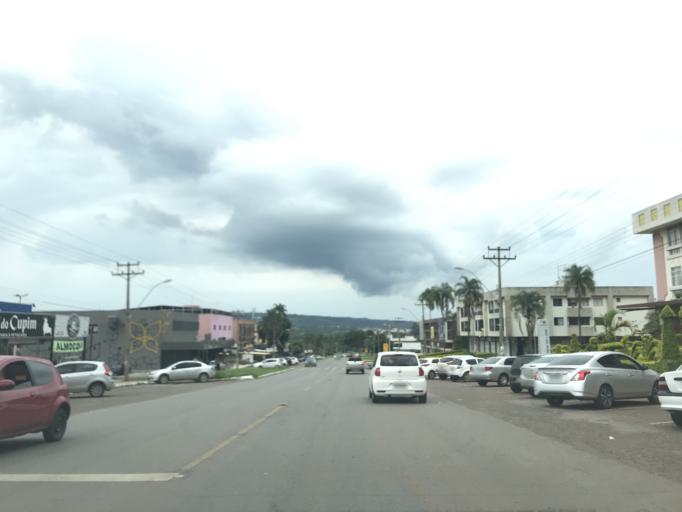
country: BR
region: Federal District
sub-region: Brasilia
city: Brasilia
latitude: -15.6560
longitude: -47.8082
